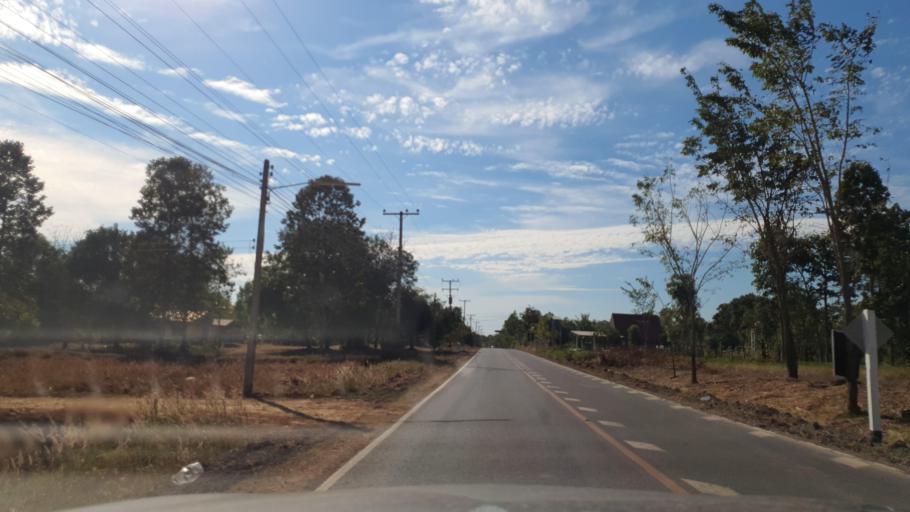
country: TH
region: Kalasin
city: Kuchinarai
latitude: 16.5426
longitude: 104.0899
